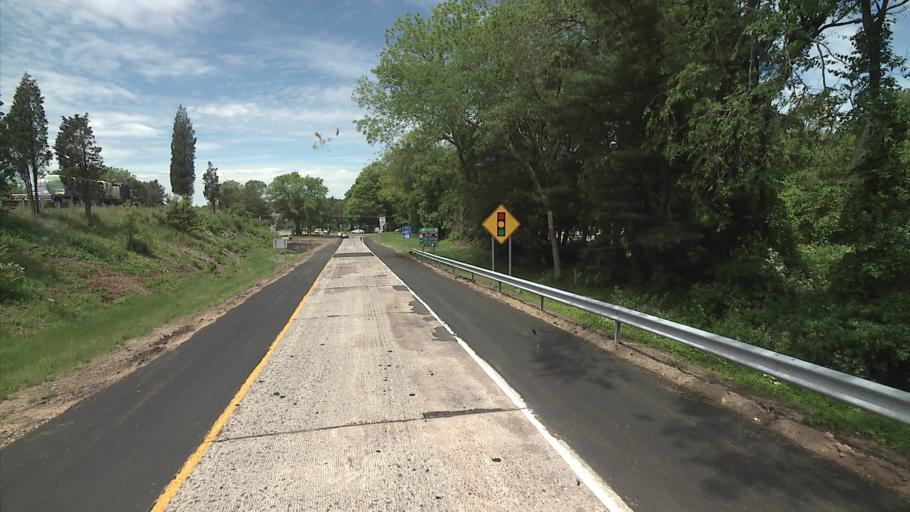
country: US
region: Connecticut
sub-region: Middlesex County
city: Old Saybrook Center
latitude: 41.3236
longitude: -72.3257
